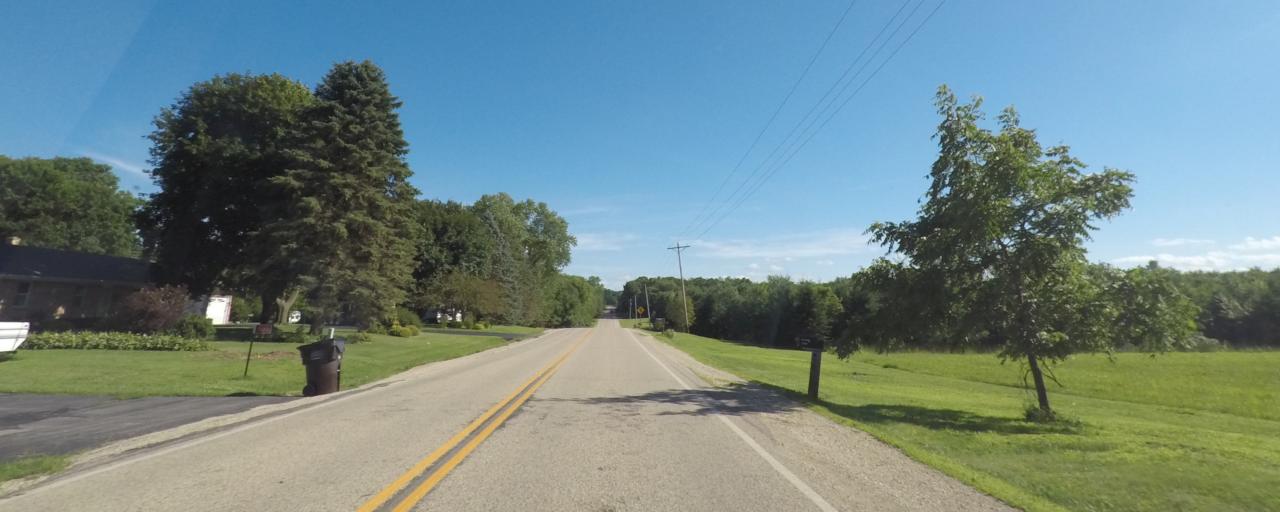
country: US
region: Wisconsin
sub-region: Rock County
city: Edgerton
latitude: 42.7551
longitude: -89.1310
